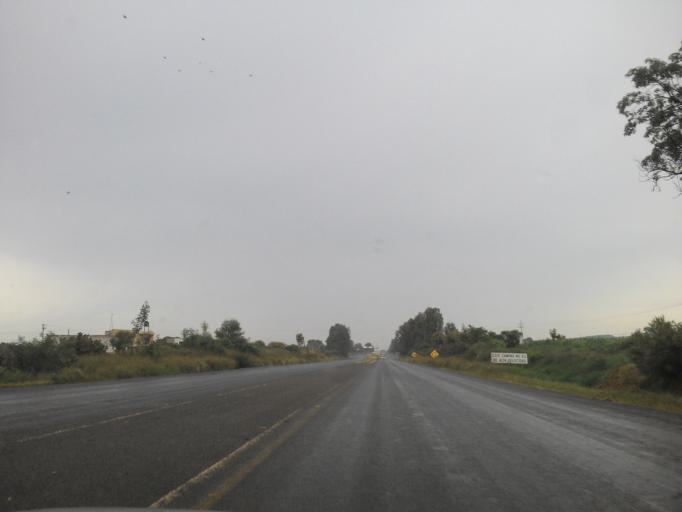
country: MX
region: Jalisco
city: Tepatitlan de Morelos
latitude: 20.8823
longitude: -102.6976
